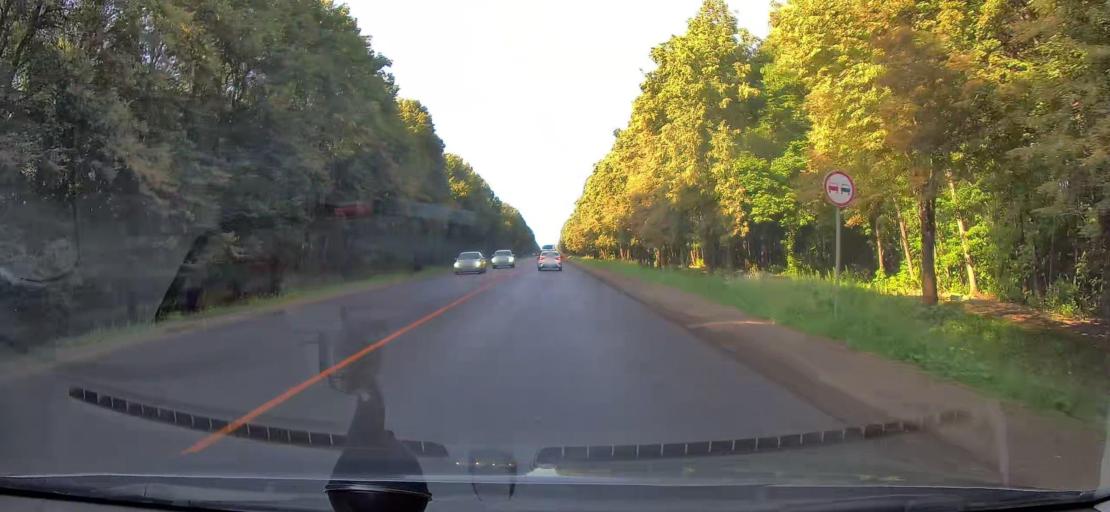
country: RU
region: Orjol
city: Spasskoye-Lutovinovo
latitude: 53.3646
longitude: 36.7271
